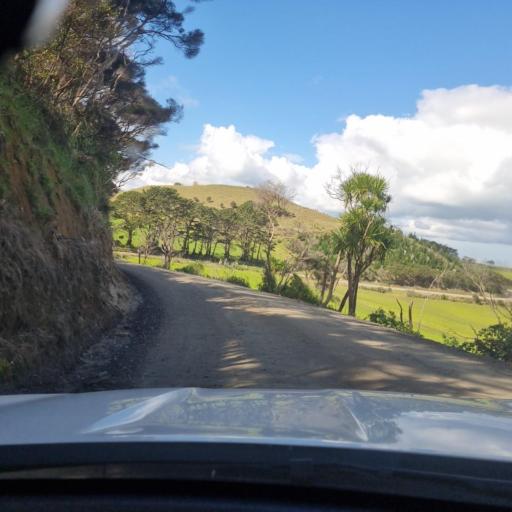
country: NZ
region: Auckland
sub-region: Auckland
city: Wellsford
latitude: -36.3226
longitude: 174.1355
